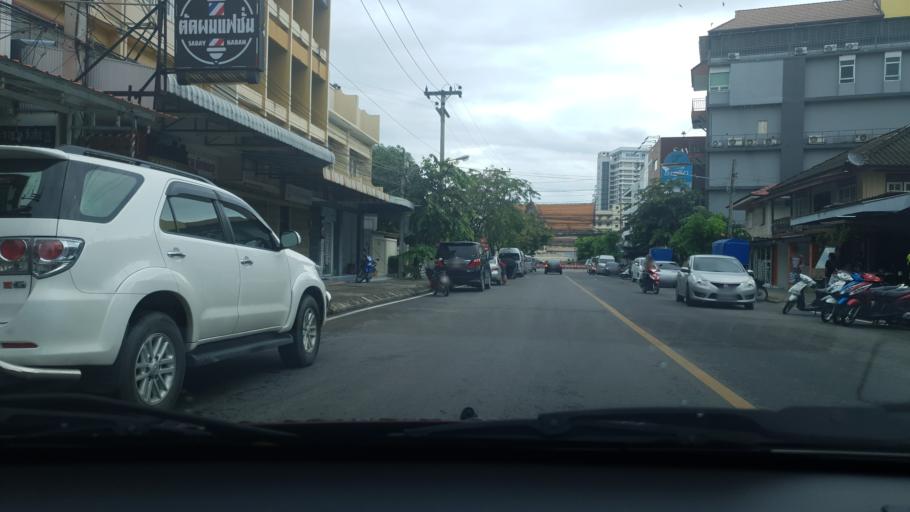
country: TH
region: Prachuap Khiri Khan
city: Hua Hin
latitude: 12.5696
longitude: 99.9561
